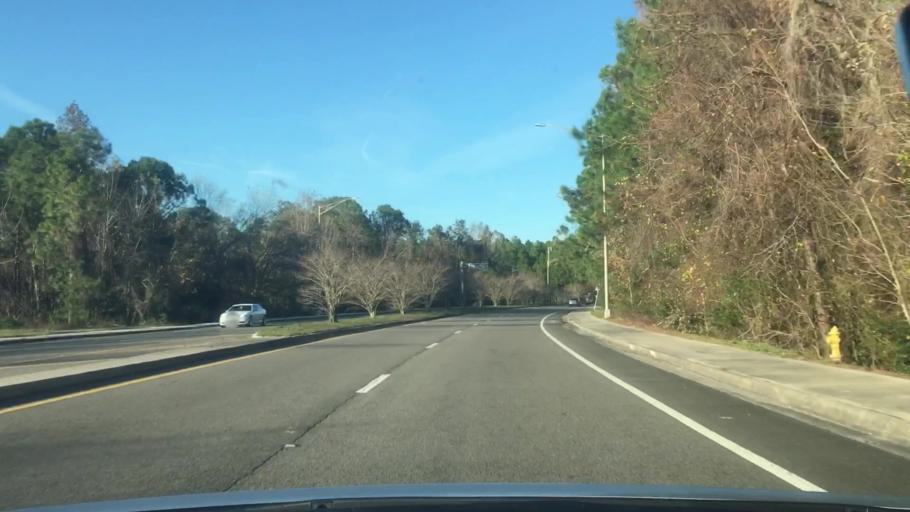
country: US
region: Florida
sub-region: Duval County
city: Jacksonville Beach
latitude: 30.2706
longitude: -81.5241
